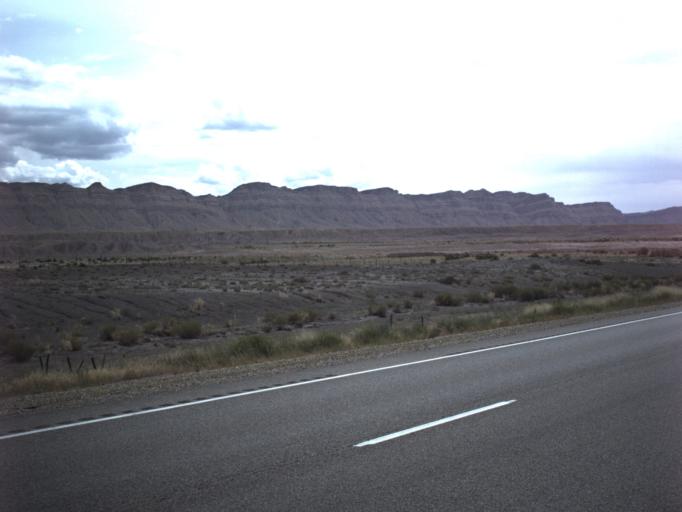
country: US
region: Utah
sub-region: Carbon County
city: East Carbon City
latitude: 39.3370
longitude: -110.3711
